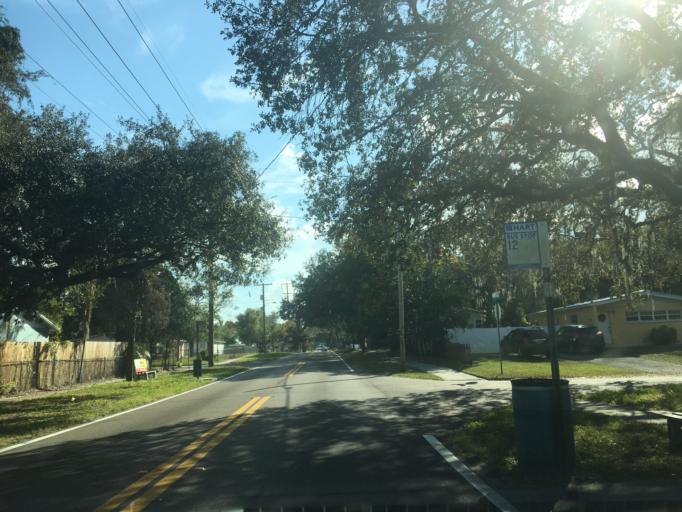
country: US
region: Florida
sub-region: Hillsborough County
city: University
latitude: 28.0375
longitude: -82.4347
